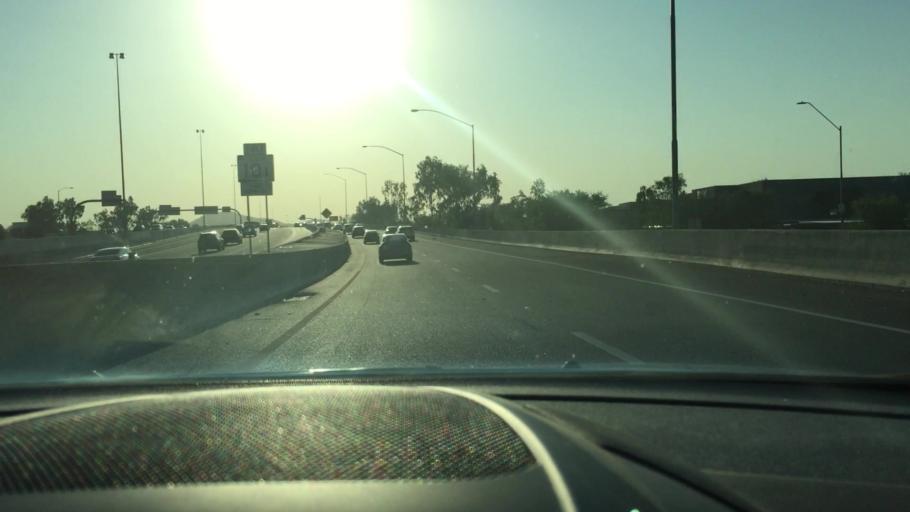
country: US
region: Arizona
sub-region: Maricopa County
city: Glendale
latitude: 33.6681
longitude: -112.1045
